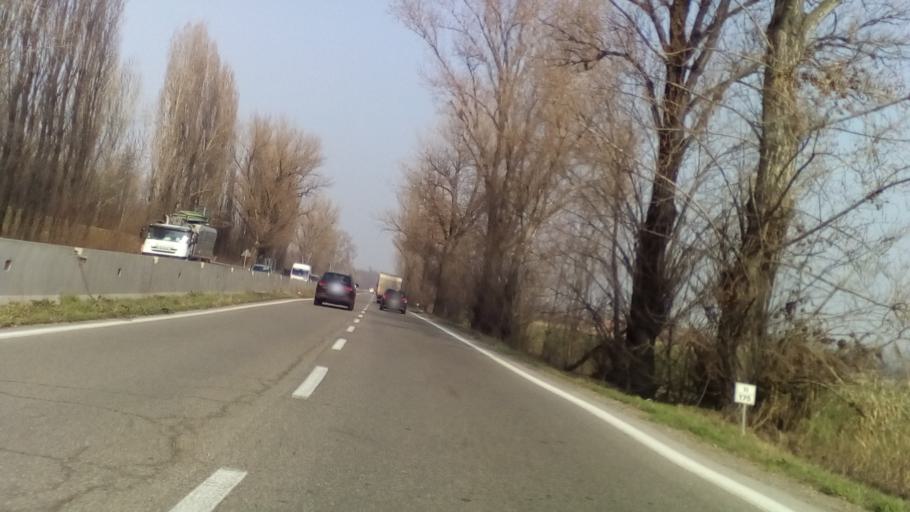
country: IT
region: Emilia-Romagna
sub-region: Provincia di Modena
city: Modena
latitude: 44.6176
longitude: 10.9416
